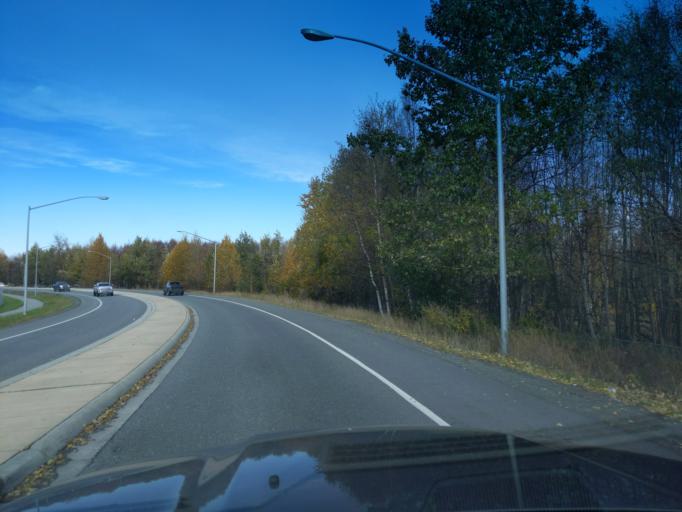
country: US
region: Alaska
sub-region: Anchorage Municipality
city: Anchorage
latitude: 61.1696
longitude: -149.9386
